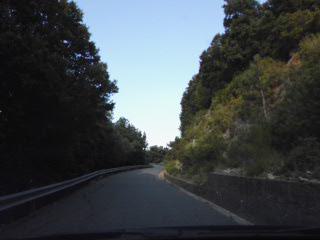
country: IT
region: Calabria
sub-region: Provincia di Vibo-Valentia
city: Nardodipace
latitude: 38.4343
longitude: 16.3403
